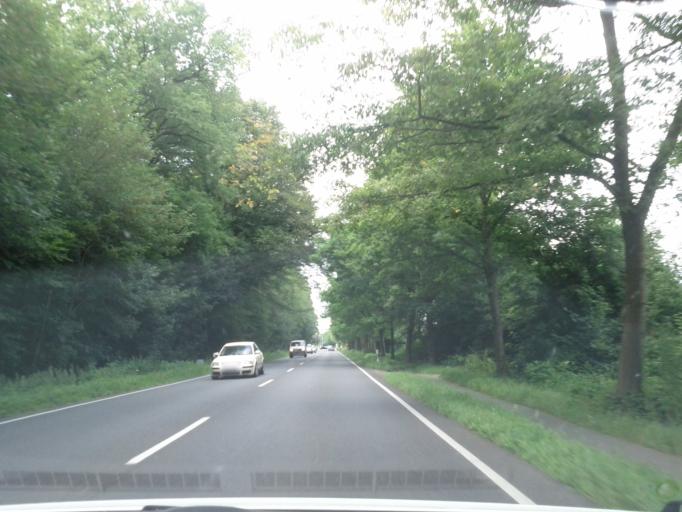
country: DE
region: Lower Saxony
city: Himmelpforten
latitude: 53.6076
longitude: 9.3163
